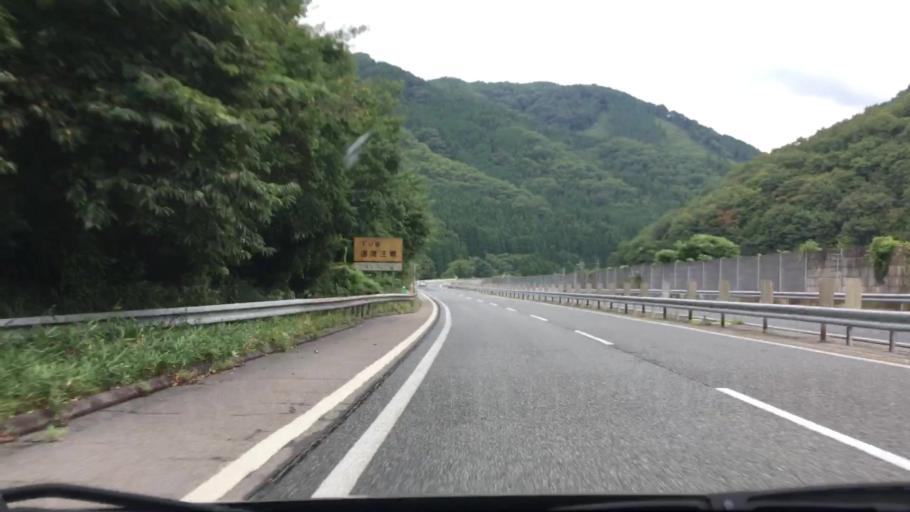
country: JP
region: Okayama
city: Niimi
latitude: 35.0096
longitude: 133.4921
